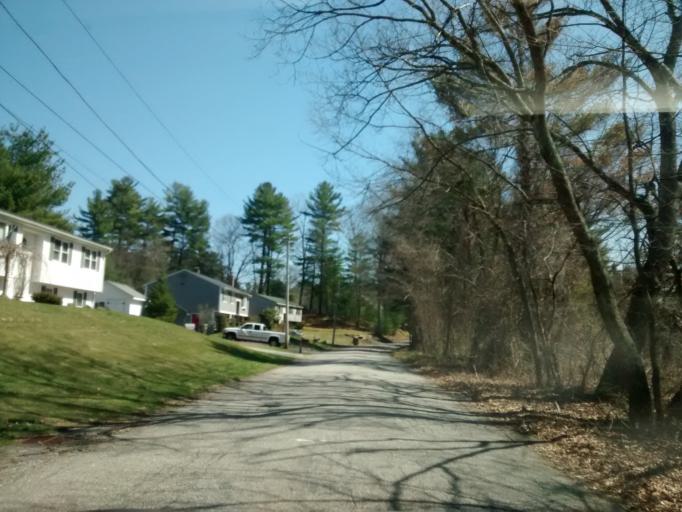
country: US
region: Massachusetts
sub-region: Worcester County
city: Oxford
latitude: 42.1162
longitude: -71.8764
